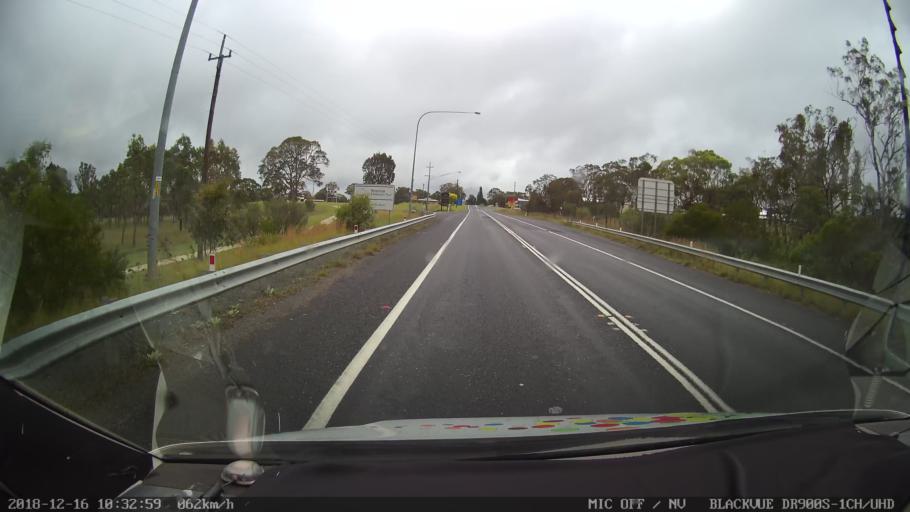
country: AU
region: New South Wales
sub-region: Tenterfield Municipality
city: Carrolls Creek
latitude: -29.0677
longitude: 152.0145
